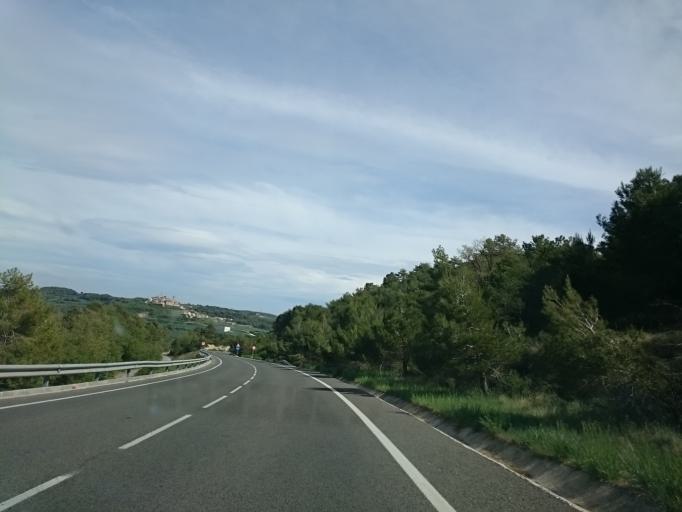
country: ES
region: Catalonia
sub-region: Provincia de Tarragona
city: Santa Coloma de Queralt
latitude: 41.5593
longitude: 1.4013
